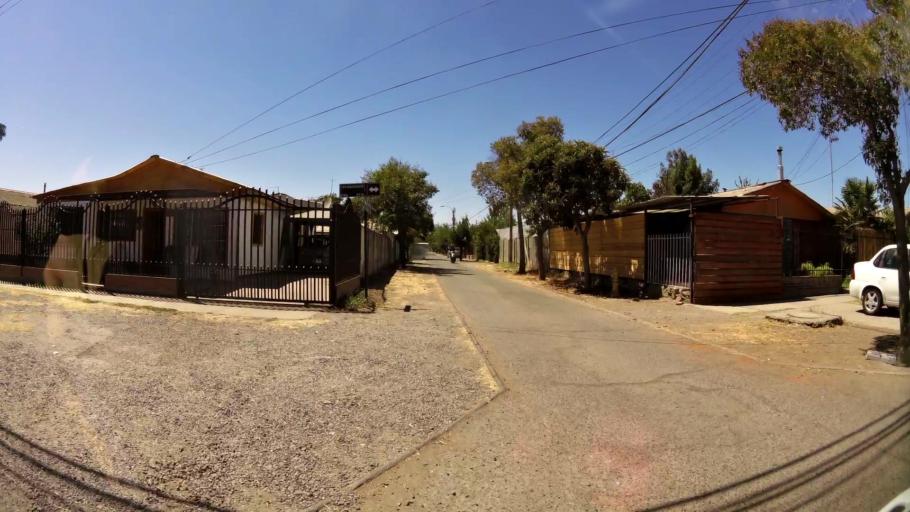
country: CL
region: O'Higgins
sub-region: Provincia de Cachapoal
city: Rancagua
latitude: -34.1618
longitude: -70.7525
